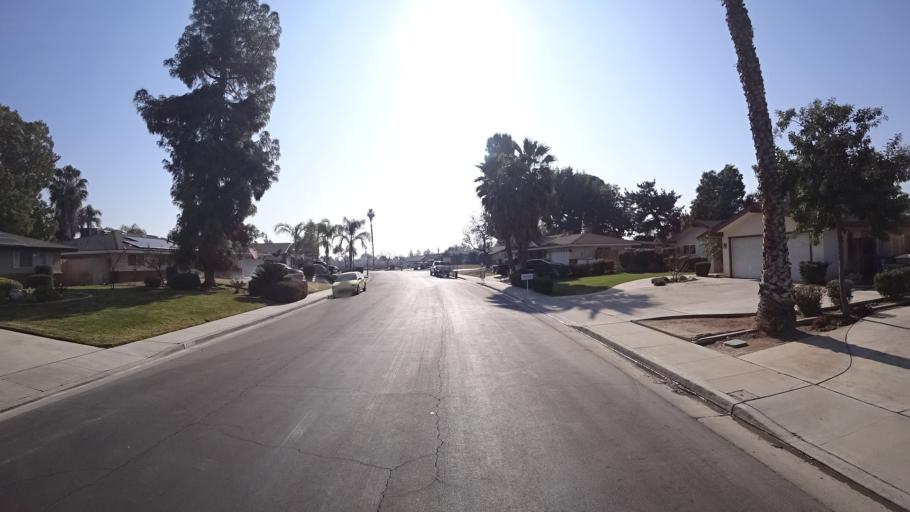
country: US
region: California
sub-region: Kern County
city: Bakersfield
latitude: 35.3305
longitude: -119.0694
